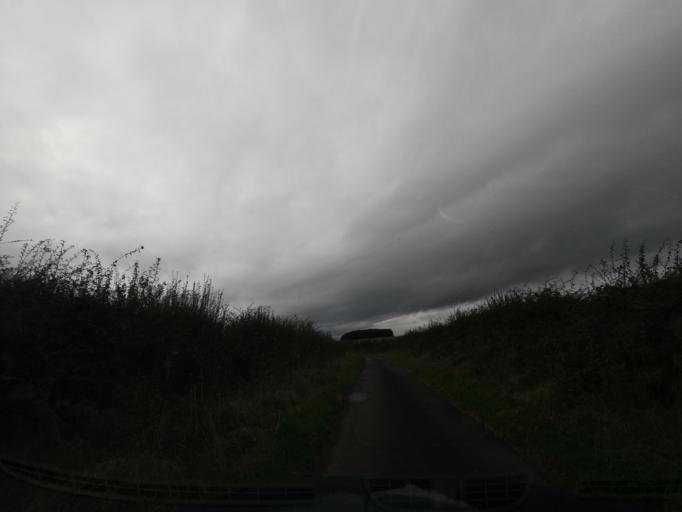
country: GB
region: England
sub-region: Northumberland
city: Ford
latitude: 55.6070
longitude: -2.0484
